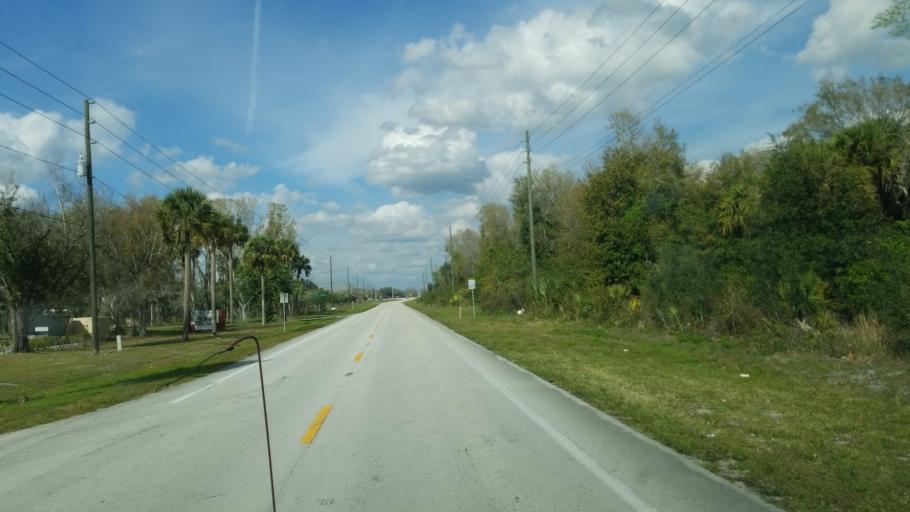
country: US
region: Florida
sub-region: Osceola County
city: Saint Cloud
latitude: 28.1385
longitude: -81.0763
